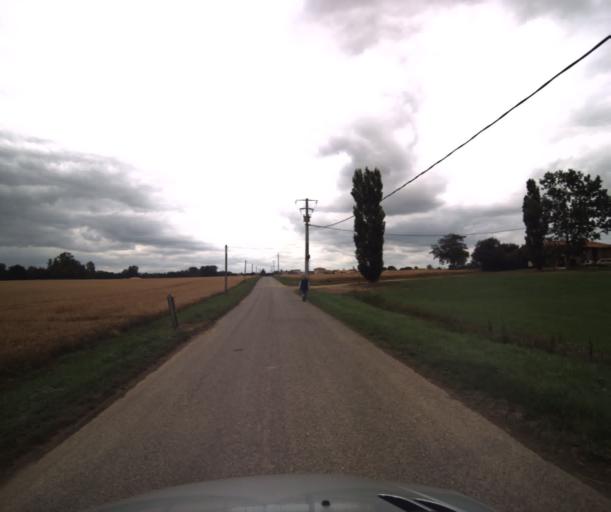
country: FR
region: Midi-Pyrenees
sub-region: Departement de la Haute-Garonne
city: Labarthe-sur-Leze
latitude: 43.4625
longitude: 1.4084
